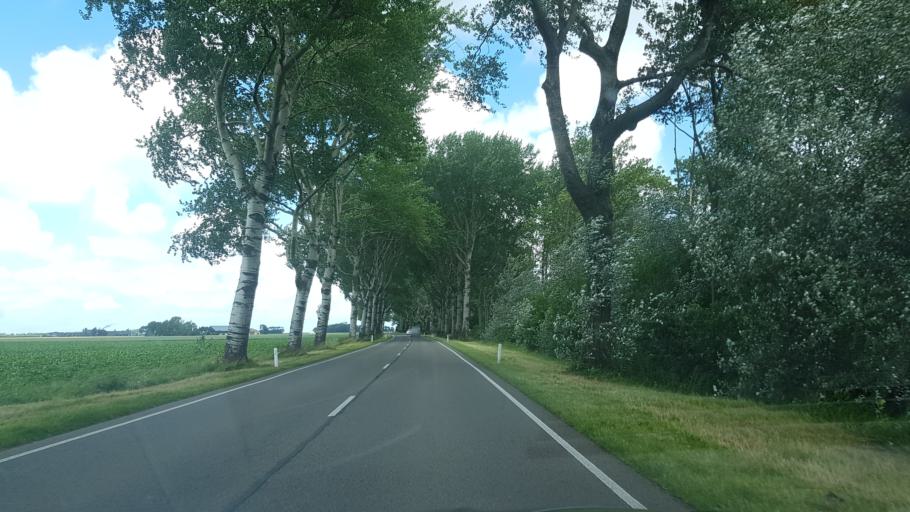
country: NL
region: Groningen
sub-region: Gemeente Winsum
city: Winsum
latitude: 53.3773
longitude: 6.5246
